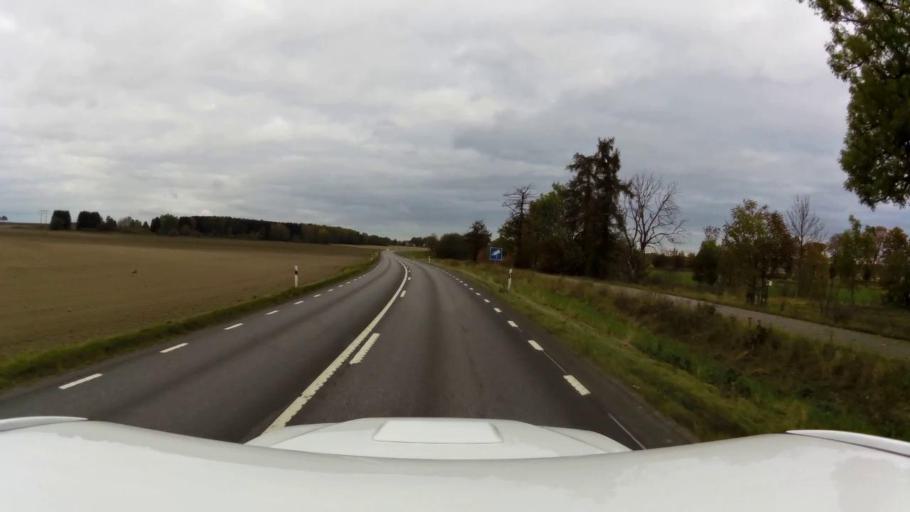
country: SE
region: OEstergoetland
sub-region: Linkopings Kommun
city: Ljungsbro
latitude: 58.5163
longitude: 15.4344
